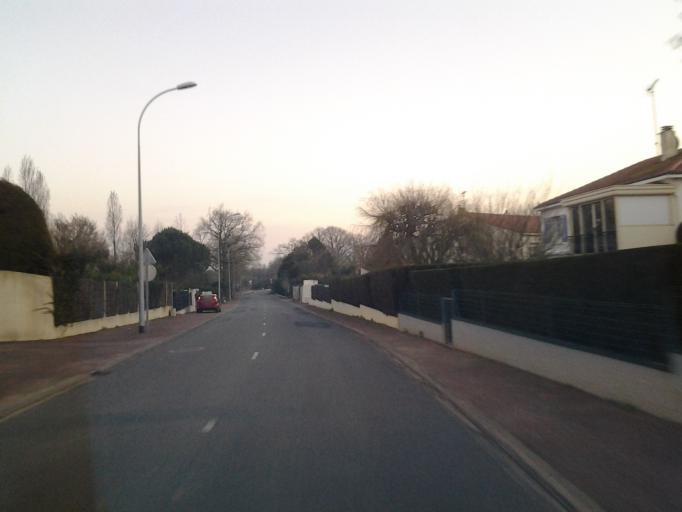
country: FR
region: Pays de la Loire
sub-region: Departement de la Vendee
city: Mouilleron-le-Captif
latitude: 46.7155
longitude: -1.4502
